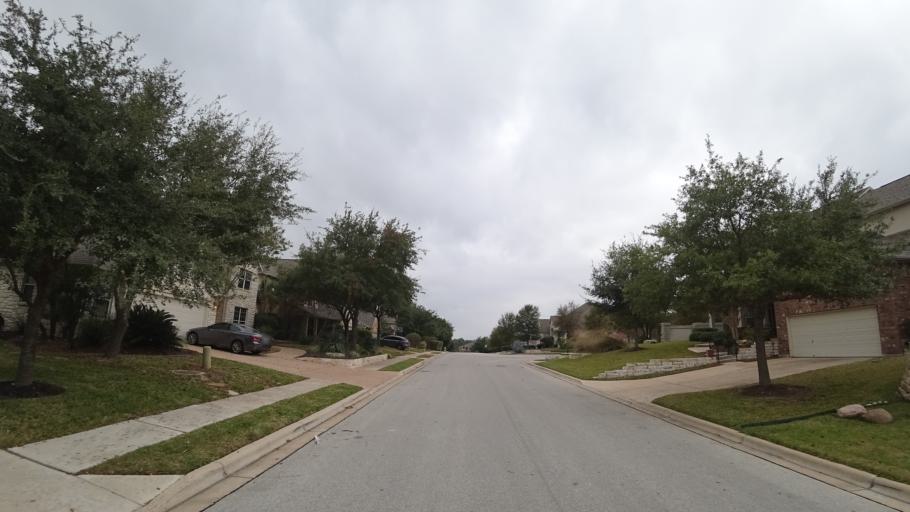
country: US
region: Texas
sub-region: Travis County
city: Hudson Bend
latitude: 30.3621
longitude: -97.8988
